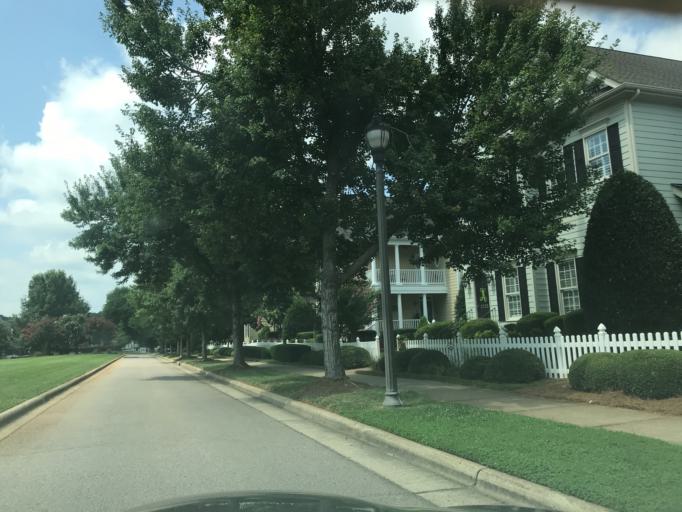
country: US
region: North Carolina
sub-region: Wake County
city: Wake Forest
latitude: 35.9271
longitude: -78.5709
